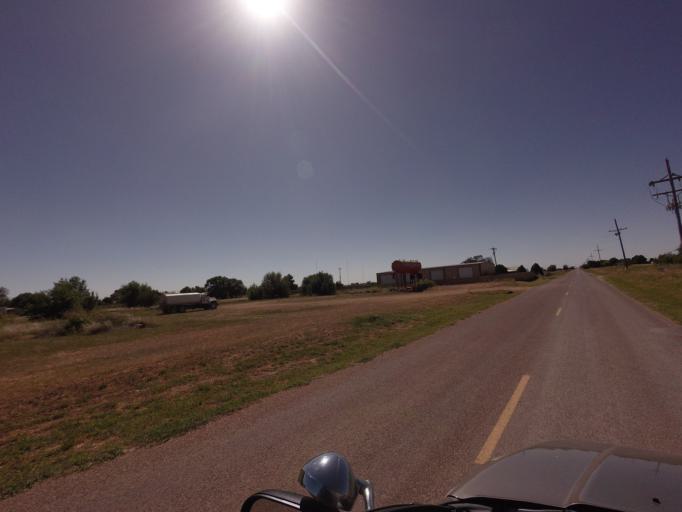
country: US
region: New Mexico
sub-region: Curry County
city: Clovis
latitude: 34.4483
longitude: -103.1985
